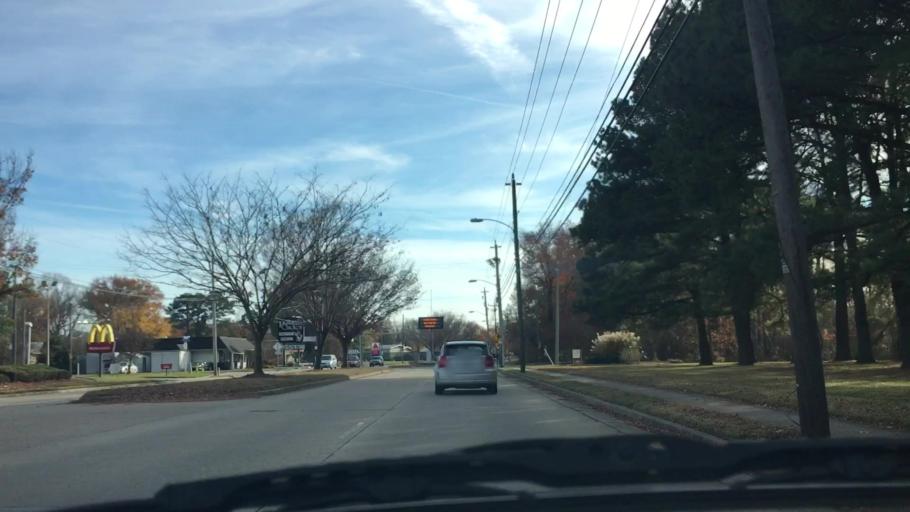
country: US
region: Virginia
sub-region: City of Norfolk
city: Norfolk
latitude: 36.9261
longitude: -76.2527
